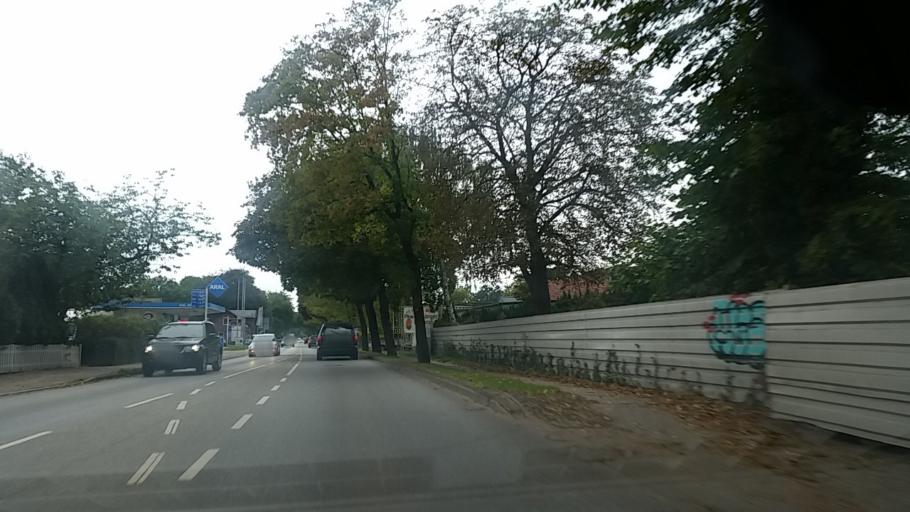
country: DE
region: Schleswig-Holstein
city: Nahe
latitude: 53.7965
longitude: 10.1418
